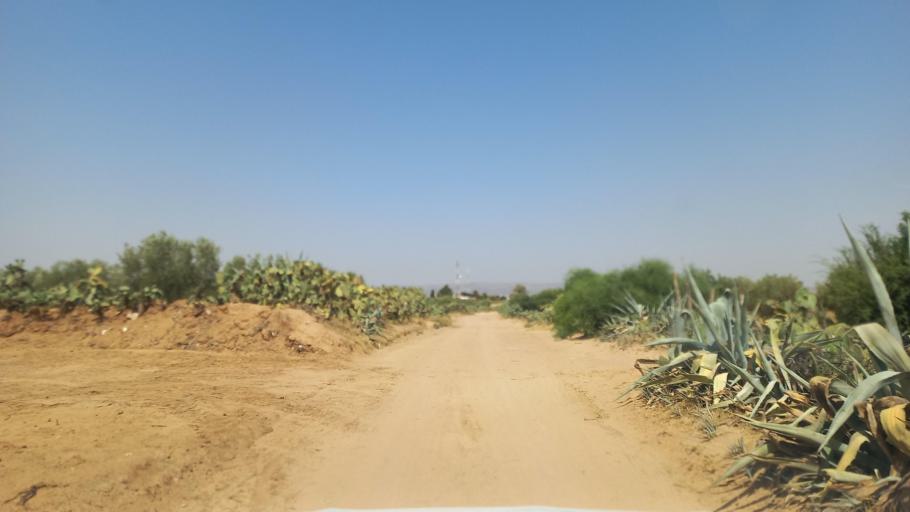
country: TN
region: Al Qasrayn
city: Kasserine
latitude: 35.2494
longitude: 9.0328
